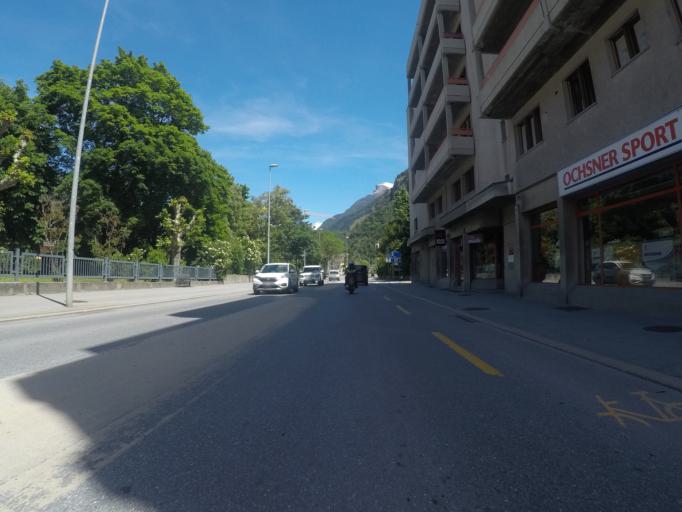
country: CH
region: Valais
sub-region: Visp District
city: Visp
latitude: 46.2924
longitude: 7.8808
